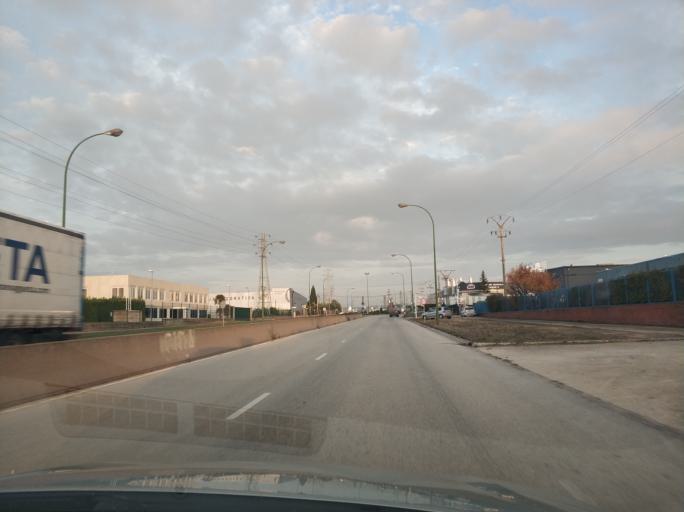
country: ES
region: Castille and Leon
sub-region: Provincia de Burgos
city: Villalbilla de Burgos
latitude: 42.3689
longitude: -3.7390
